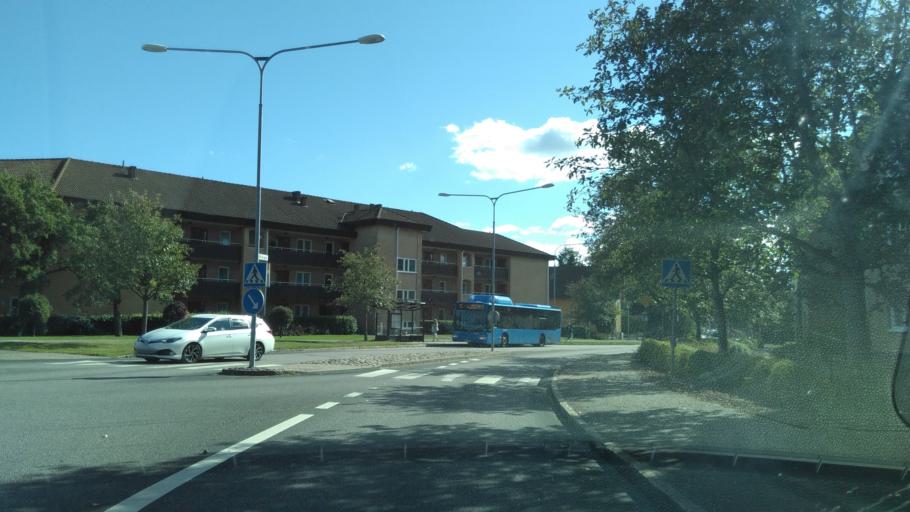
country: SE
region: Vaestra Goetaland
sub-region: Skovde Kommun
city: Skoevde
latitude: 58.3975
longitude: 13.8436
